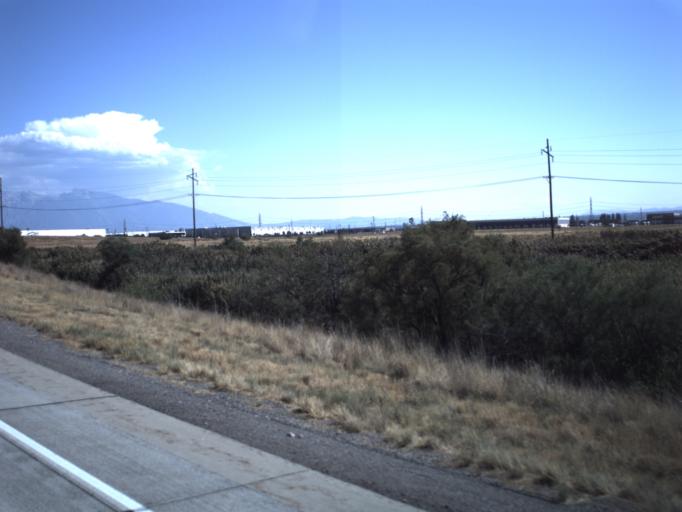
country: US
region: Utah
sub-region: Salt Lake County
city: West Valley City
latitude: 40.7703
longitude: -112.0294
